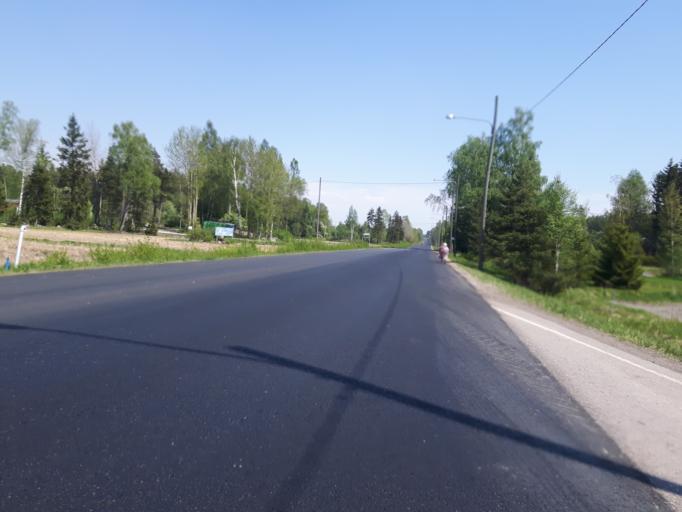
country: FI
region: Uusimaa
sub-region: Helsinki
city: Nickby
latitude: 60.3172
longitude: 25.4045
